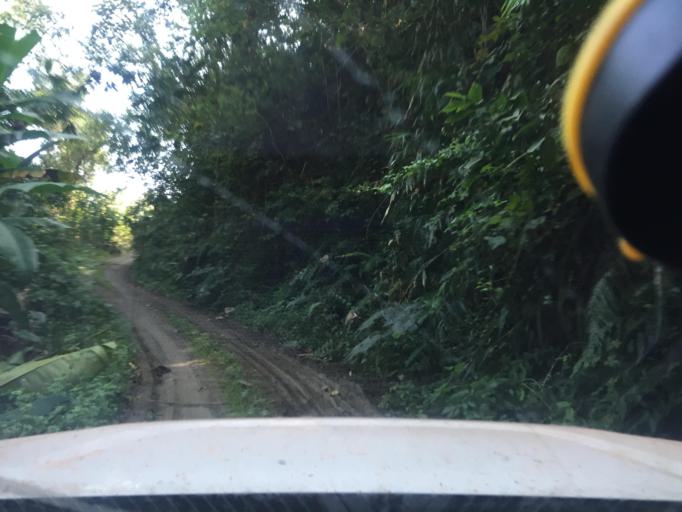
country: LA
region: Phongsali
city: Phongsali
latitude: 21.6890
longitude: 102.4084
